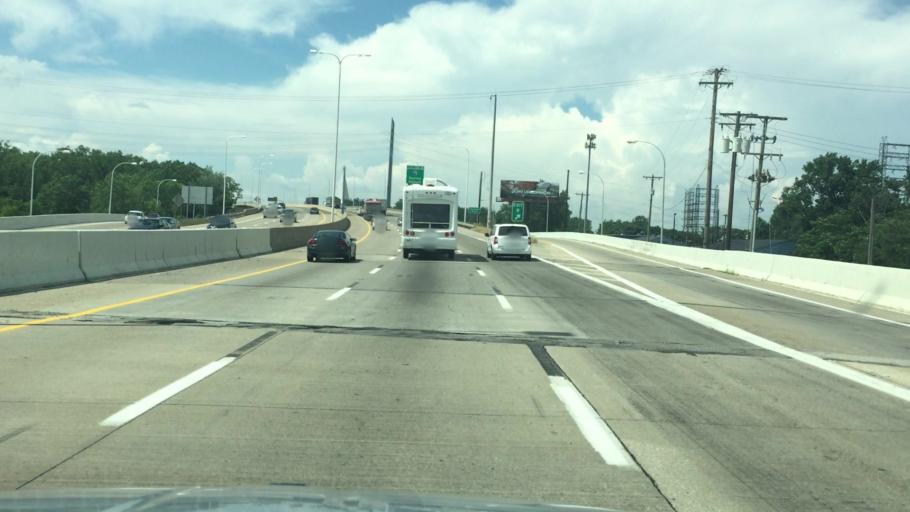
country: US
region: Ohio
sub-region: Lucas County
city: Oregon
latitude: 41.6501
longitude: -83.5017
